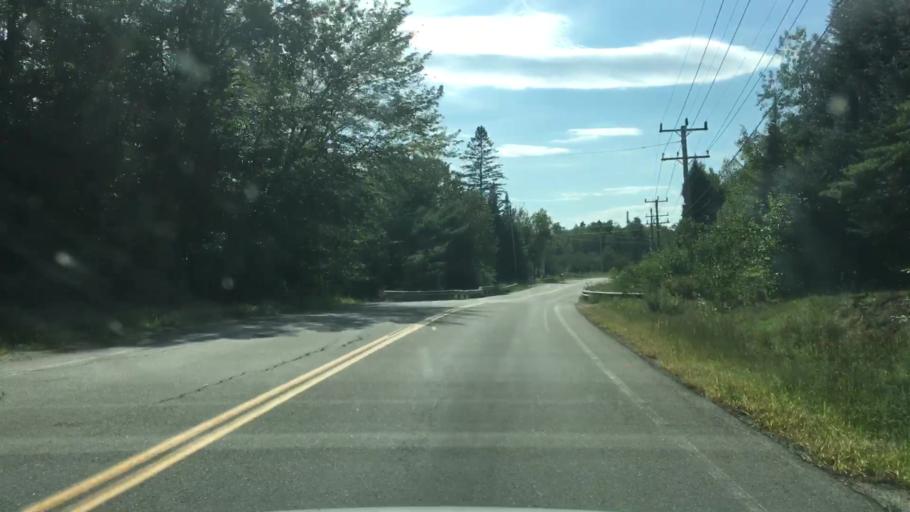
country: US
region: Maine
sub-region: Penobscot County
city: Lincoln
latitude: 45.3936
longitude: -68.5177
